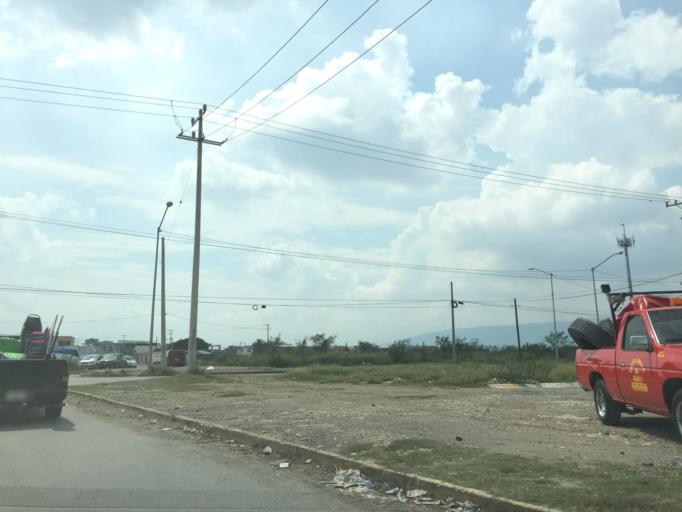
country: MX
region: Nuevo Leon
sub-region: Apodaca
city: Fraccionamiento Cosmopolis Octavo Sector
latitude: 25.8095
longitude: -100.2640
